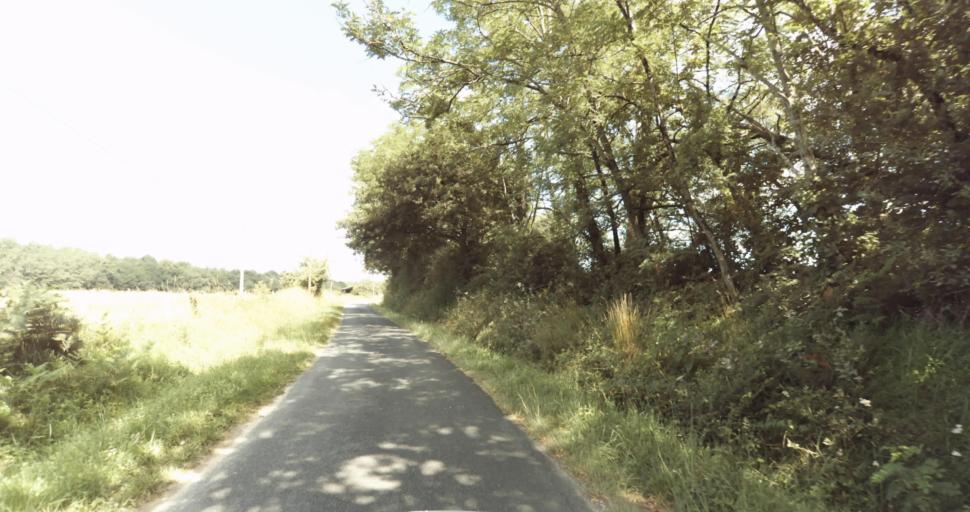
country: FR
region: Aquitaine
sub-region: Departement de la Gironde
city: Bazas
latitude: 44.4544
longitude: -0.2168
